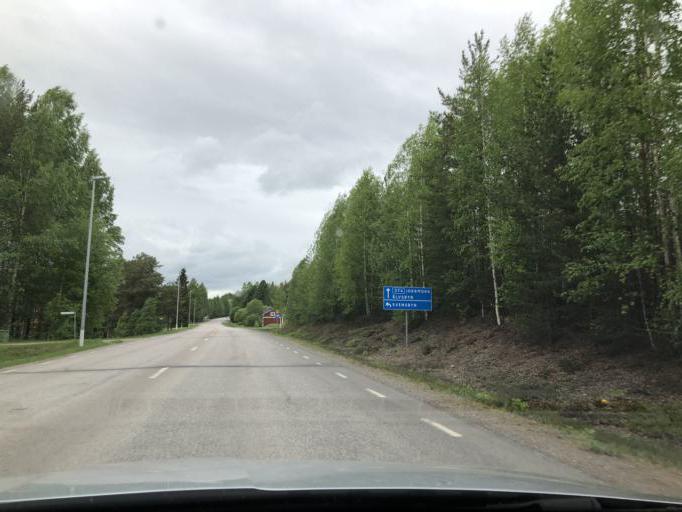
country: SE
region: Norrbotten
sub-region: Pitea Kommun
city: Bergsviken
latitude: 65.3834
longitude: 21.3340
